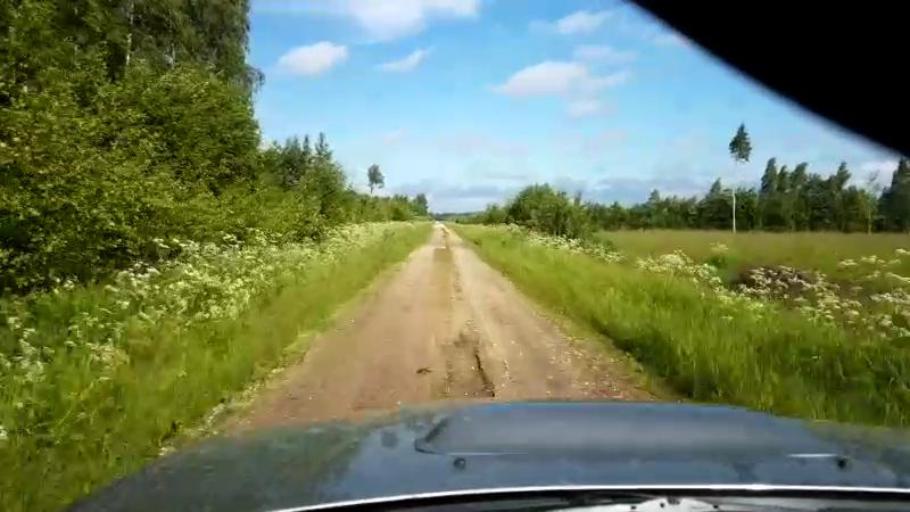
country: EE
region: Paernumaa
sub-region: Sindi linn
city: Sindi
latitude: 58.4873
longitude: 24.6605
